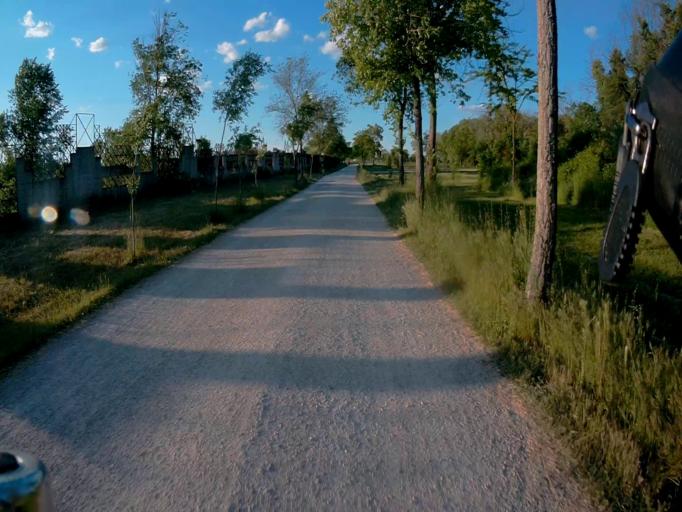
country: ES
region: Madrid
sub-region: Provincia de Madrid
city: Alcorcon
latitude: 40.3280
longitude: -3.8050
